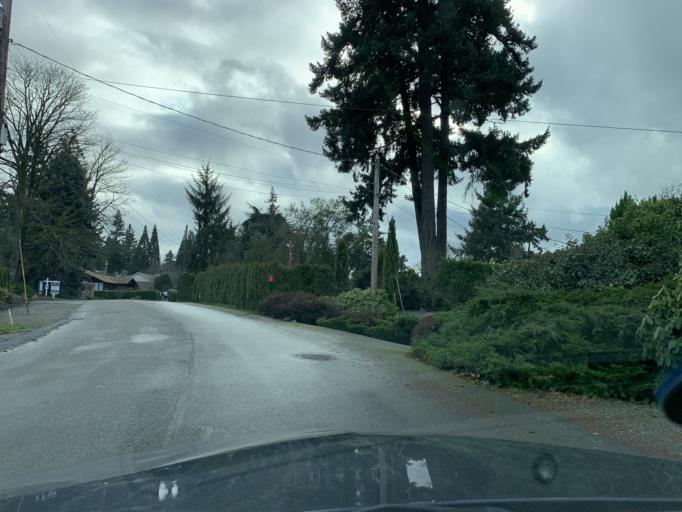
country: US
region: Washington
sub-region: King County
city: Mercer Island
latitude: 47.5869
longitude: -122.2451
